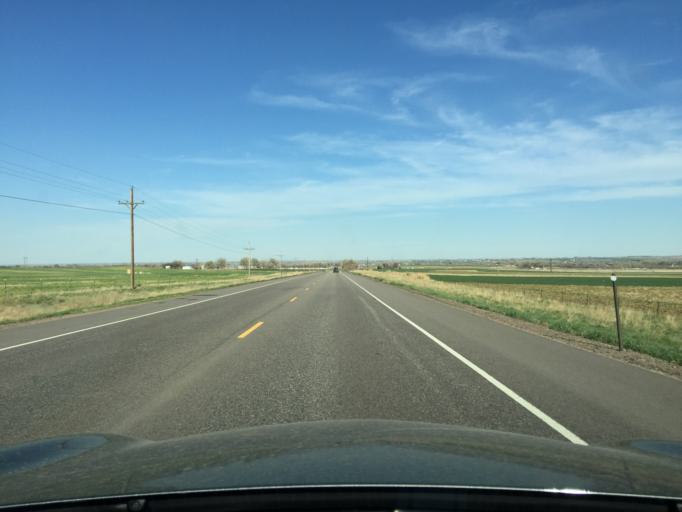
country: US
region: Colorado
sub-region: Boulder County
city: Niwot
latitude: 40.0874
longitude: -105.1224
